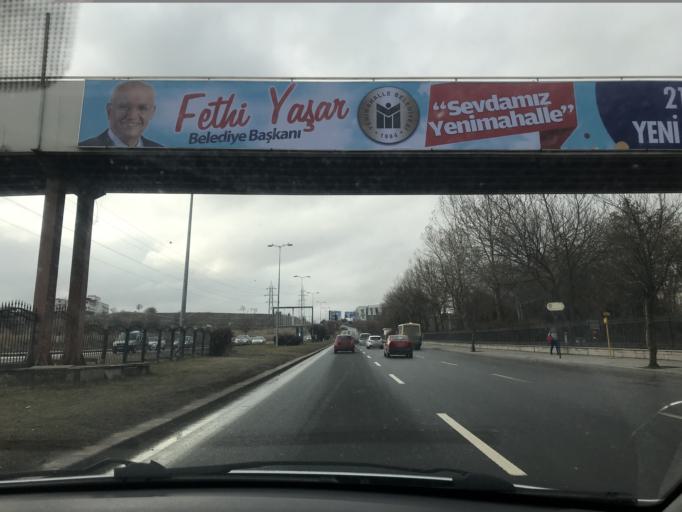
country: TR
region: Ankara
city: Batikent
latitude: 39.9588
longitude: 32.7871
